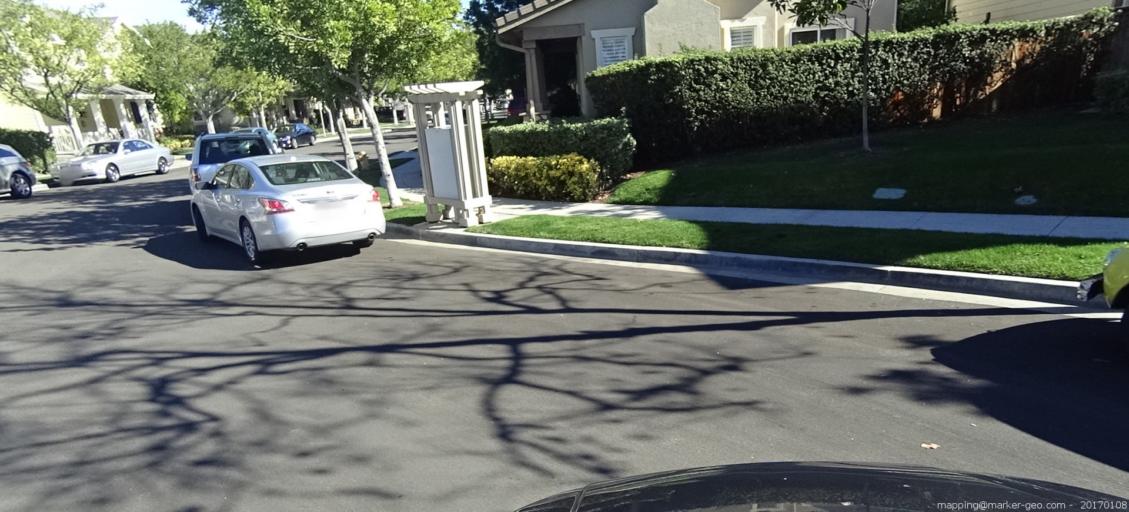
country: US
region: California
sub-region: Orange County
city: Ladera Ranch
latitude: 33.5679
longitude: -117.6378
